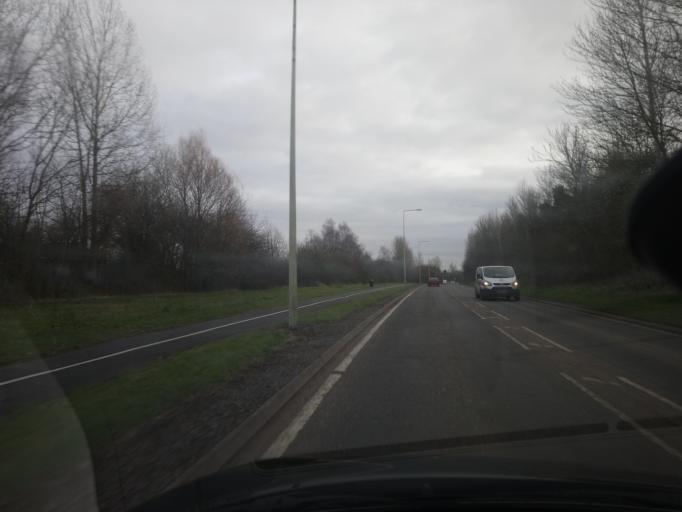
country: GB
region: England
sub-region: Telford and Wrekin
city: Telford
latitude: 52.6738
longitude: -2.4642
